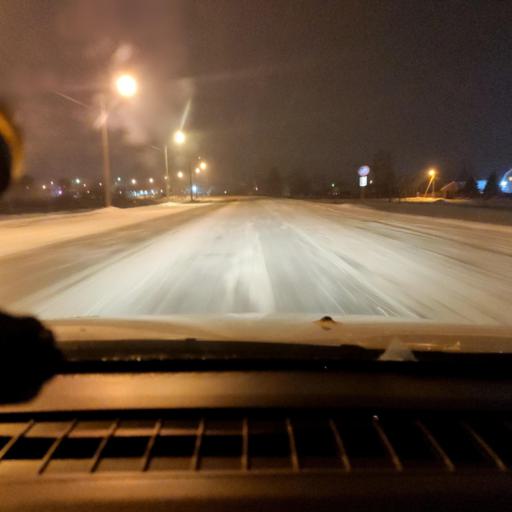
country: RU
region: Samara
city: Georgiyevka
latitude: 53.2689
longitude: 51.0027
